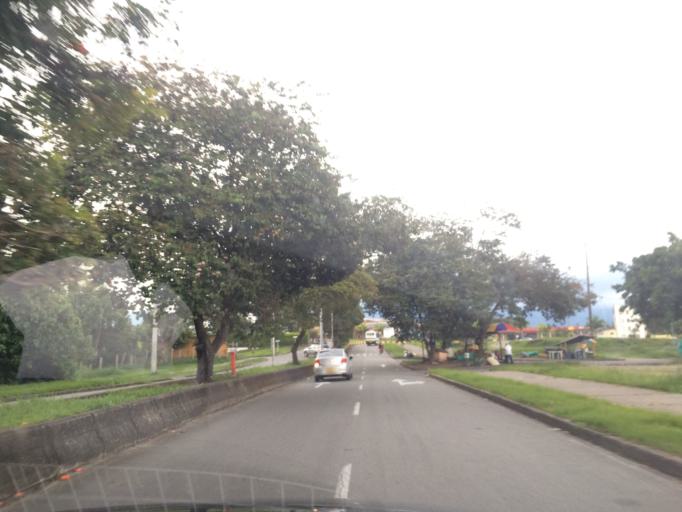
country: CO
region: Quindio
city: Armenia
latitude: 4.5172
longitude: -75.6972
